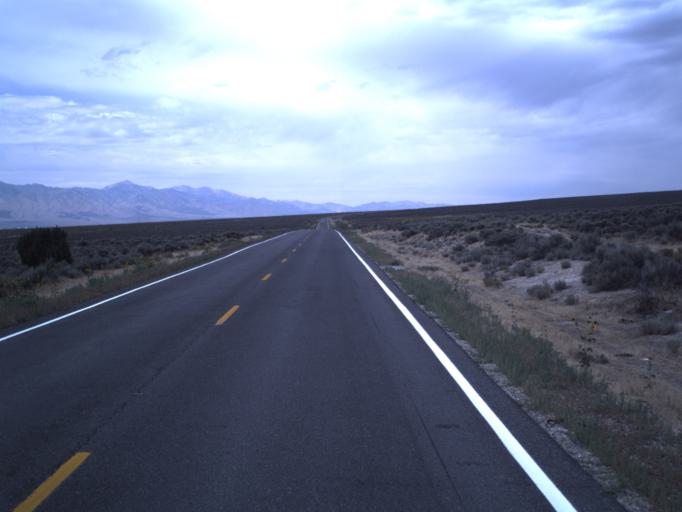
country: US
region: Utah
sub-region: Tooele County
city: Tooele
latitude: 40.2812
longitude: -112.2583
